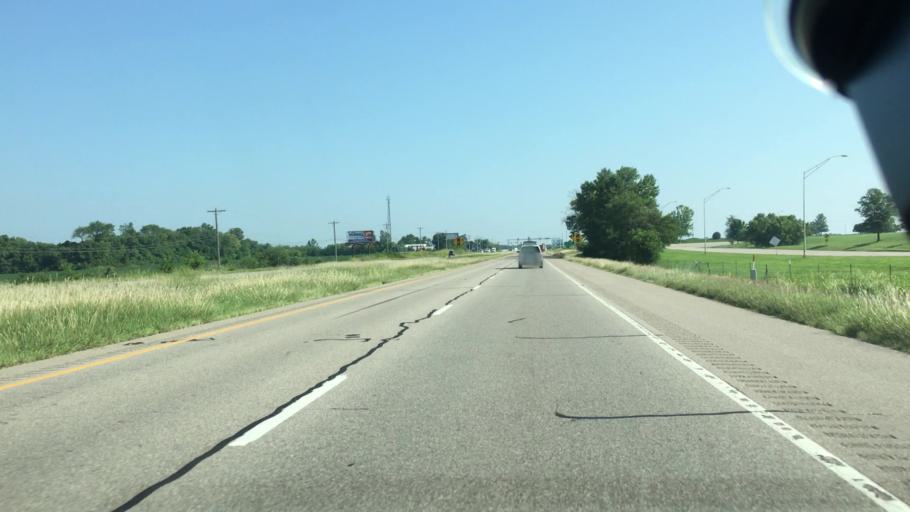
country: US
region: Indiana
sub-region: Gibson County
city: Fort Branch
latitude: 38.2990
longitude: -87.5674
